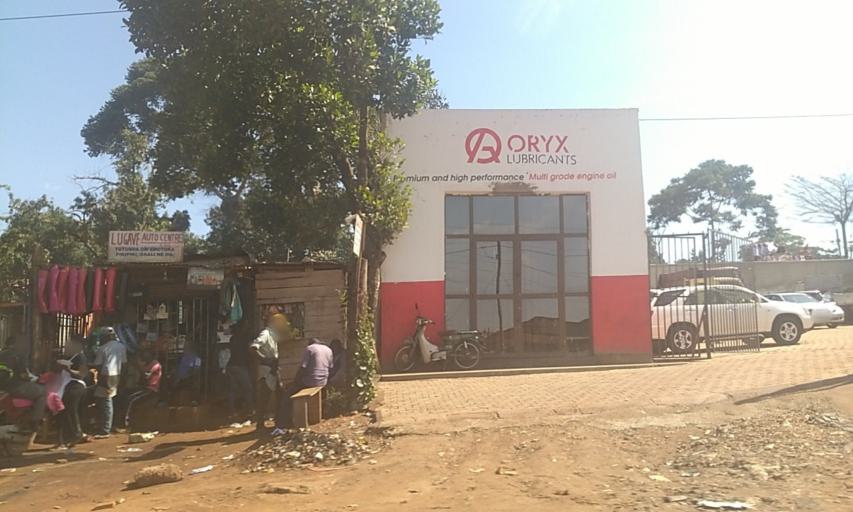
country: UG
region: Central Region
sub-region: Wakiso District
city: Kireka
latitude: 0.3445
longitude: 32.6418
